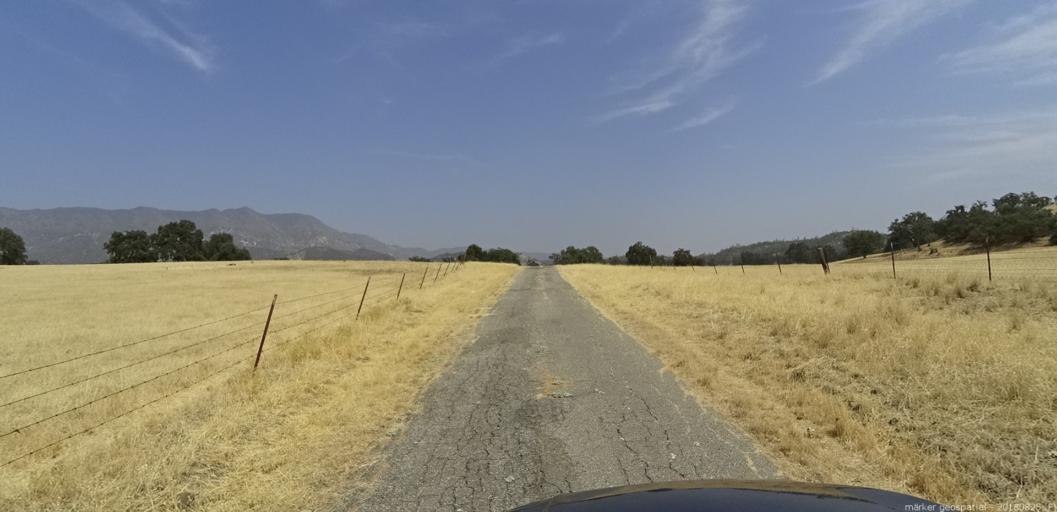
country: US
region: California
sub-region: Fresno County
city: Coalinga
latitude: 36.1835
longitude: -120.6689
